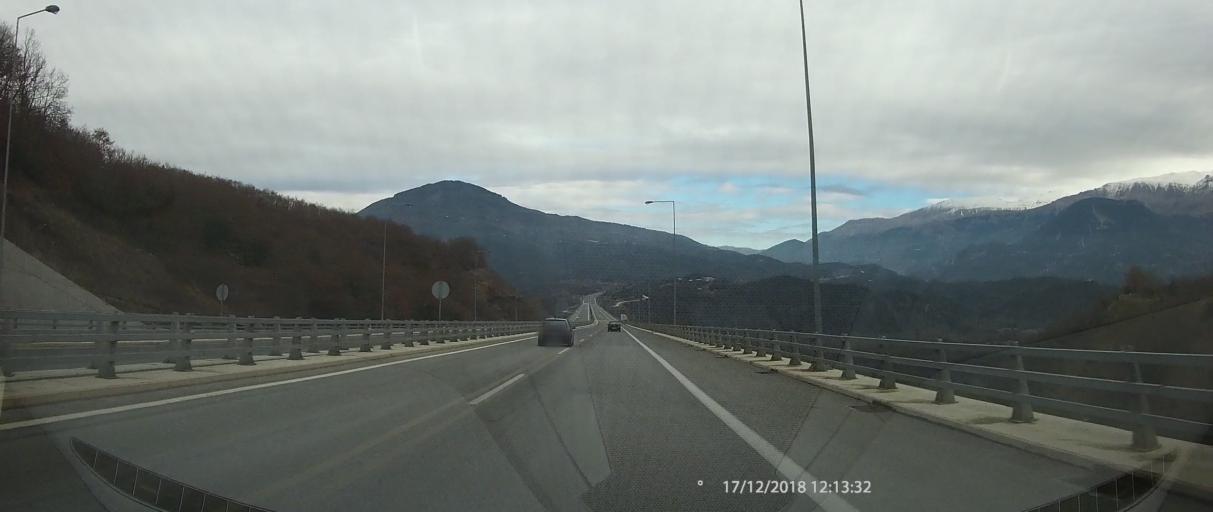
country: GR
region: Epirus
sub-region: Nomos Ioanninon
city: Katsikas
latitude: 39.7076
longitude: 20.9740
